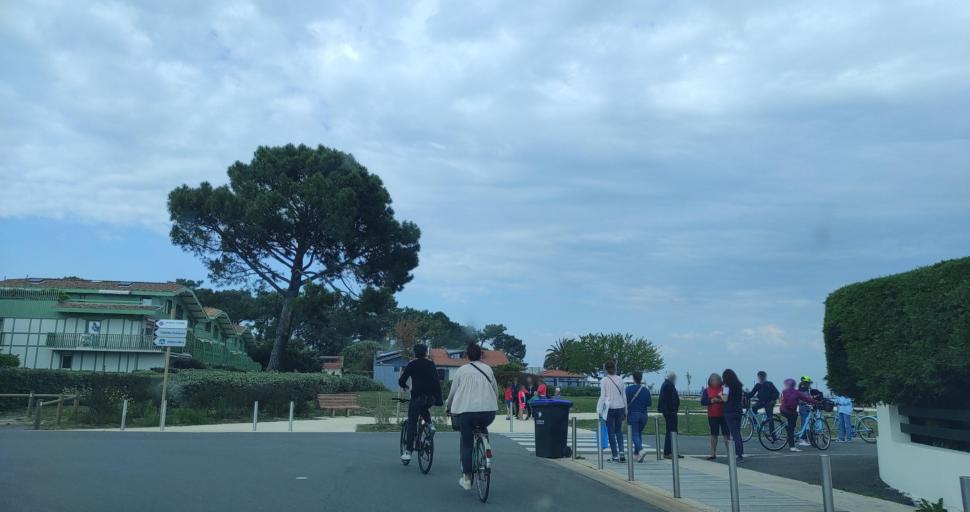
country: FR
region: Aquitaine
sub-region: Departement de la Gironde
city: Arcachon
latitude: 44.6554
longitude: -1.2405
